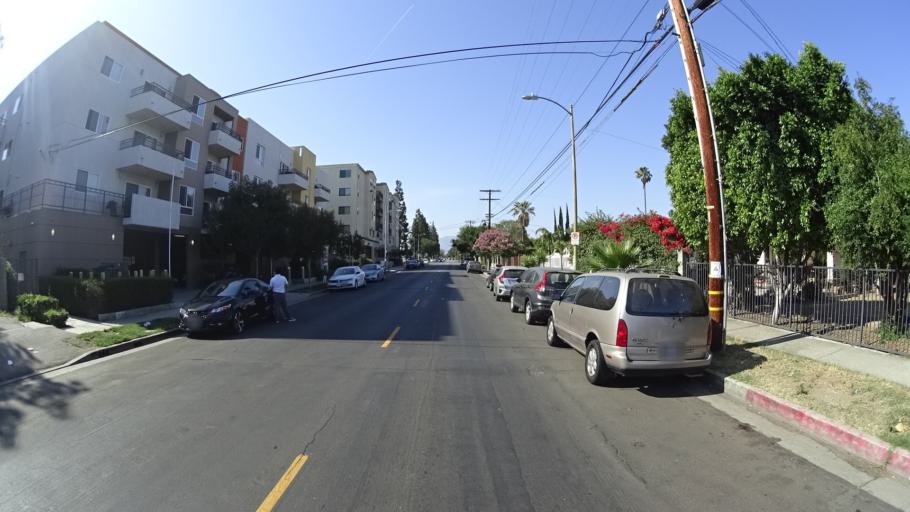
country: US
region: California
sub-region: Los Angeles County
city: Van Nuys
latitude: 34.2143
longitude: -118.4287
